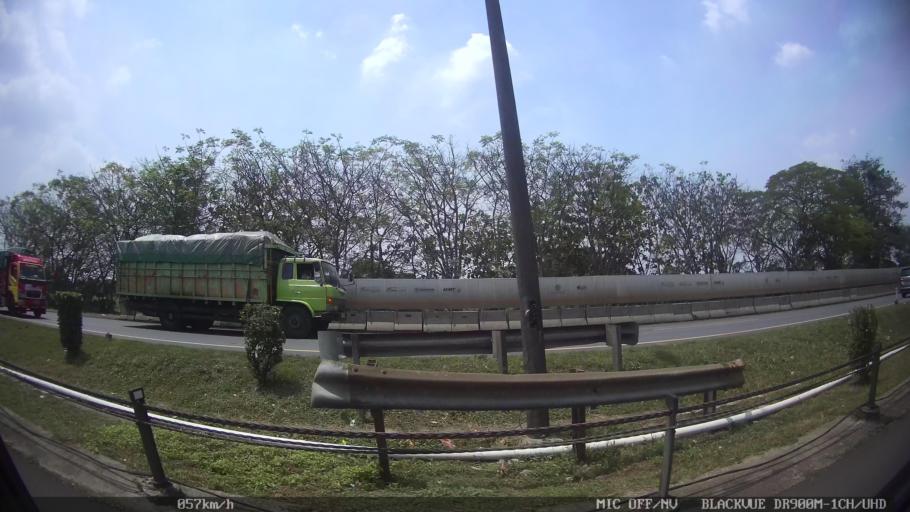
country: ID
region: Banten
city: Serang
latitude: -6.1342
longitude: 106.2100
